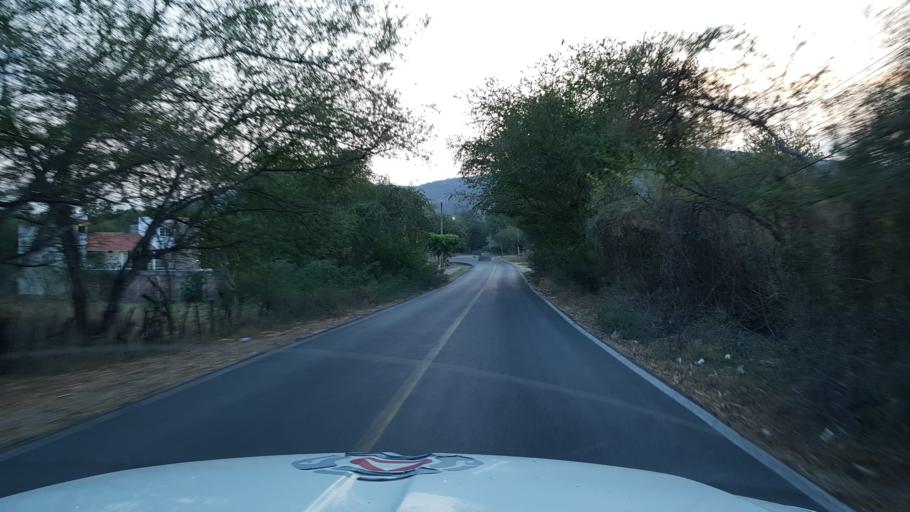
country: MX
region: Morelos
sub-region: Tlaltizapan de Zapata
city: Colonia Palo Prieto (Chipitongo)
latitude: 18.7151
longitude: -99.1081
